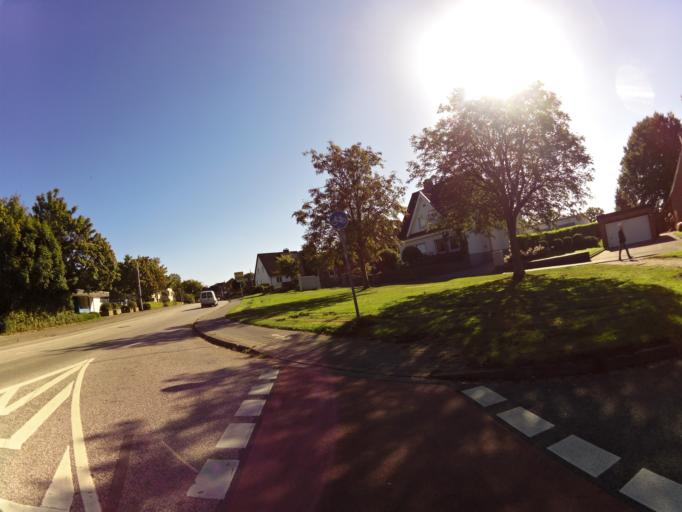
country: DE
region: Schleswig-Holstein
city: Eckernforde
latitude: 54.4555
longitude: 9.8331
